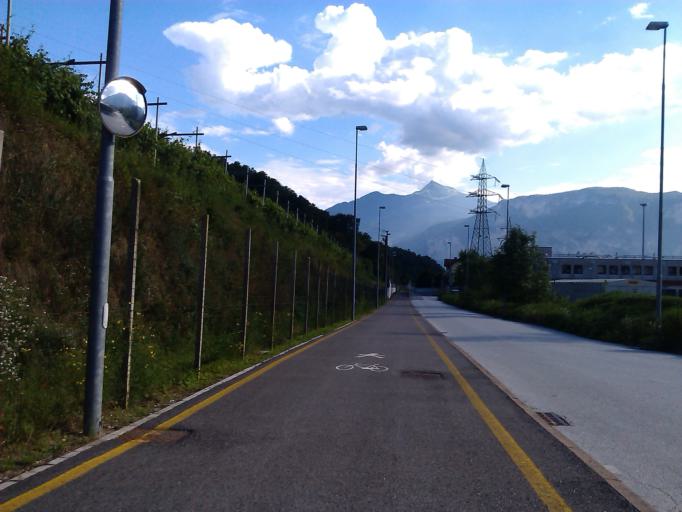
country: IT
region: Trentino-Alto Adige
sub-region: Provincia di Trento
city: Meano
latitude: 46.1318
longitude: 11.1135
